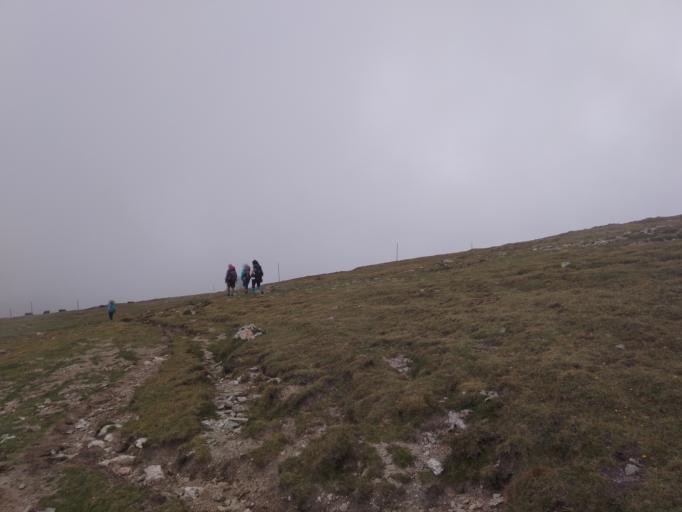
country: BG
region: Plovdiv
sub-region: Obshtina Karlovo
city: Kalofer
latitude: 42.7161
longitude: 24.9118
